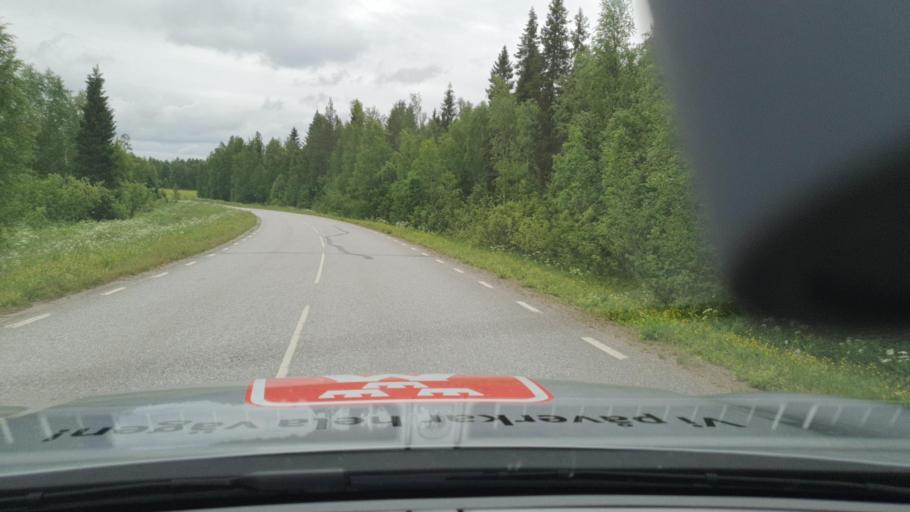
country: SE
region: Norrbotten
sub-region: Lulea Kommun
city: Ranea
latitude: 65.8829
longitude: 22.2025
